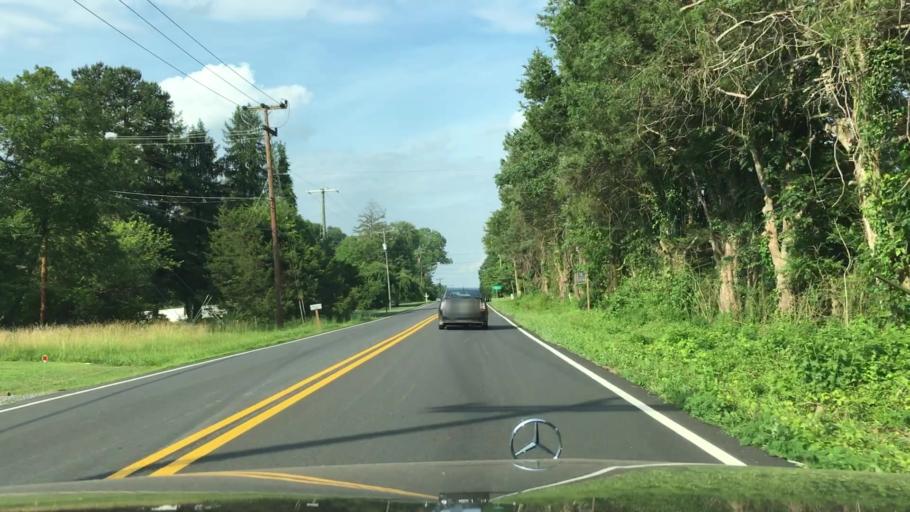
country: US
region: Virginia
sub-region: Orange County
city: Gordonsville
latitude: 38.1366
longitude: -78.1985
